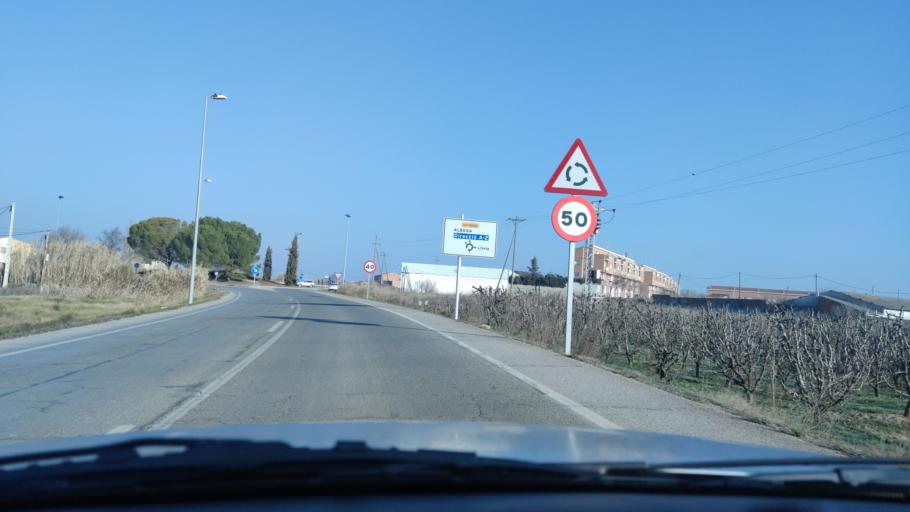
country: ES
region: Catalonia
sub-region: Provincia de Lleida
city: Lleida
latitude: 41.6449
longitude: 0.6357
